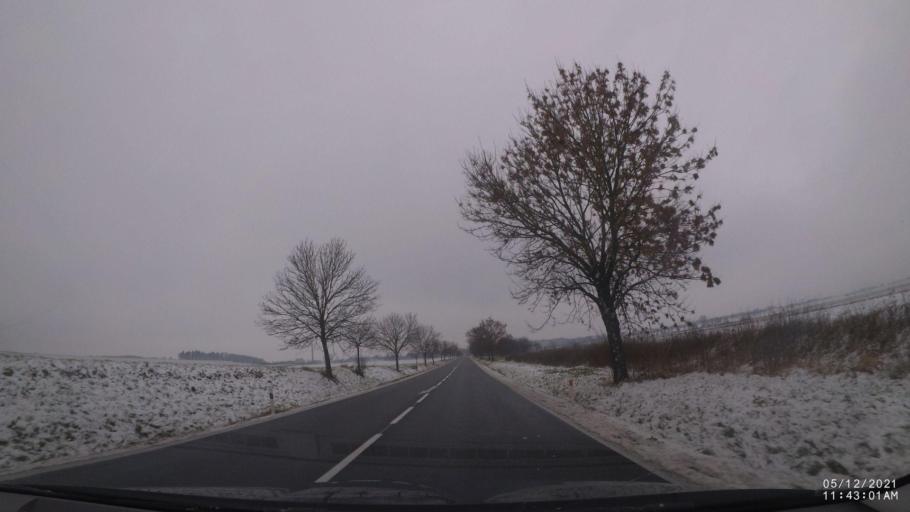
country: CZ
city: Dobruska
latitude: 50.2828
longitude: 16.1776
